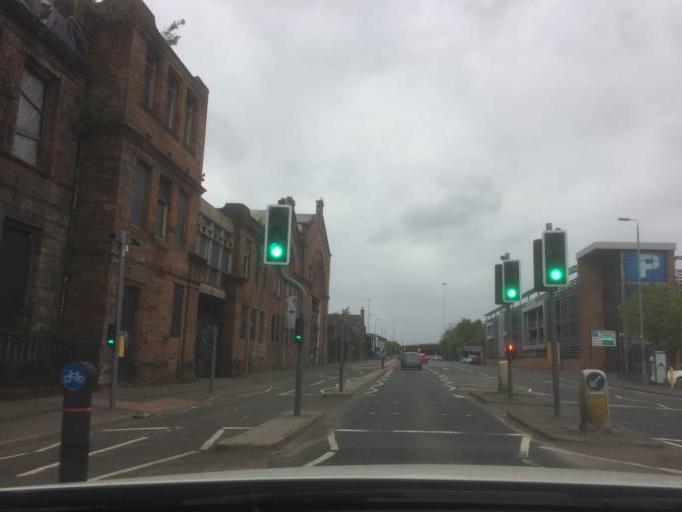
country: GB
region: Scotland
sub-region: Glasgow City
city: Glasgow
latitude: 55.8499
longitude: -4.2722
